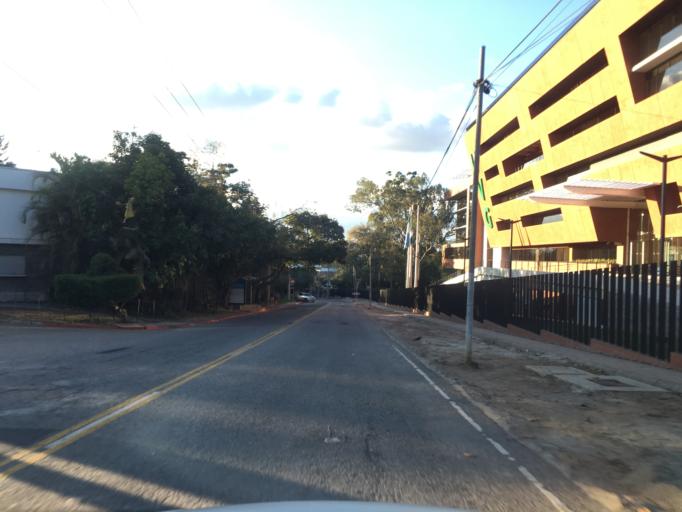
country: GT
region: Guatemala
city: Santa Catarina Pinula
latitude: 14.6040
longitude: -90.4898
